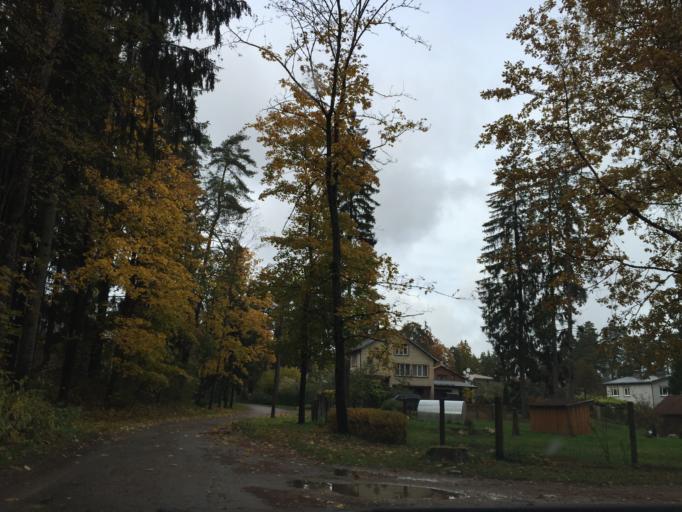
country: LV
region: Ogre
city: Ogre
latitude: 56.8091
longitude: 24.6295
